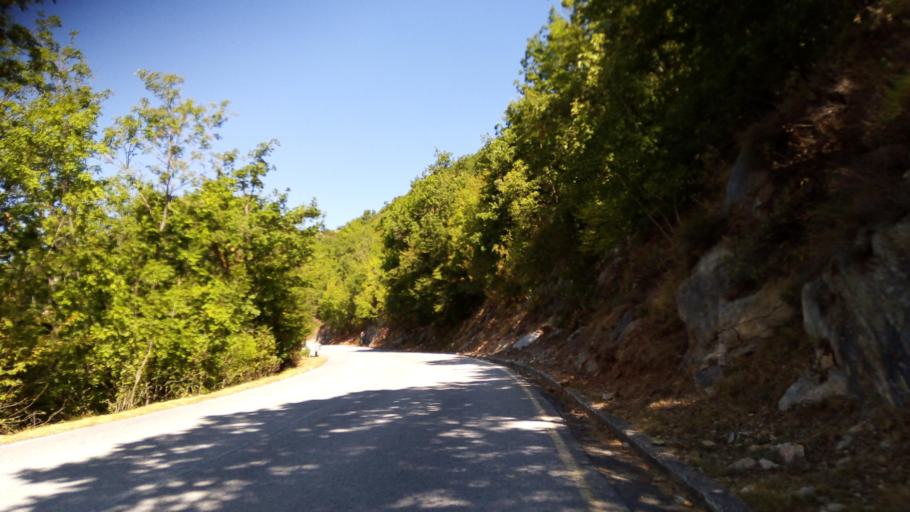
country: IT
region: Liguria
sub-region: Provincia di Savona
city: Balestrino
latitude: 44.1451
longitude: 8.1696
